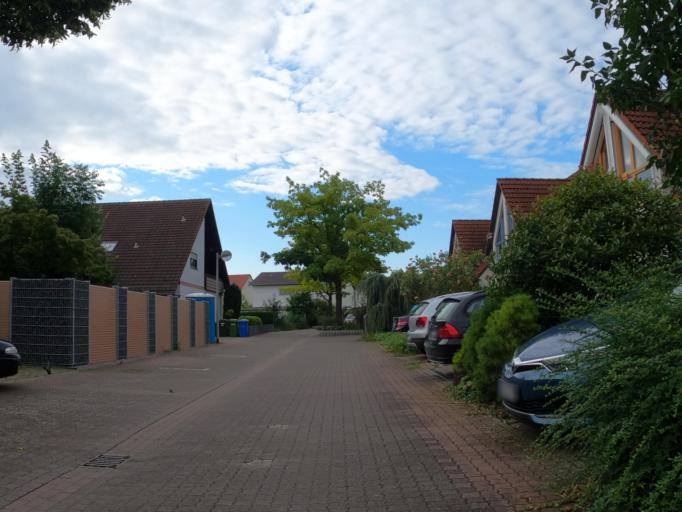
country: DE
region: Rheinland-Pfalz
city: Freinsheim
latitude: 49.5096
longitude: 8.2094
